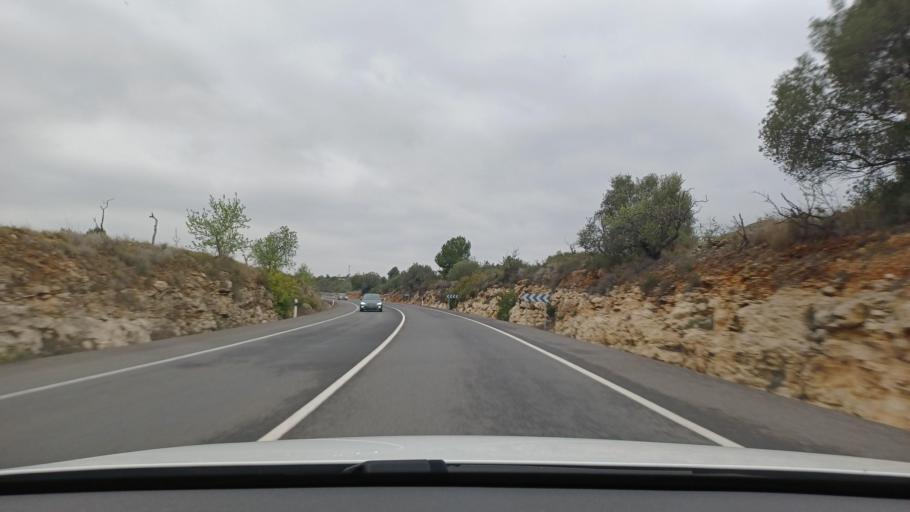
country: ES
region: Valencia
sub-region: Provincia de Castello
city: Alcala de Xivert
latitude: 40.2725
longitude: 0.2394
